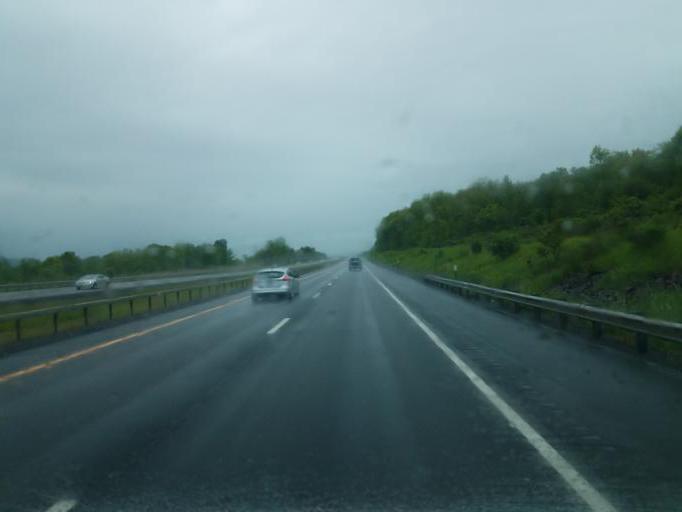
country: US
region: New York
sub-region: Herkimer County
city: Frankfort
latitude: 43.0426
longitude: -75.0541
